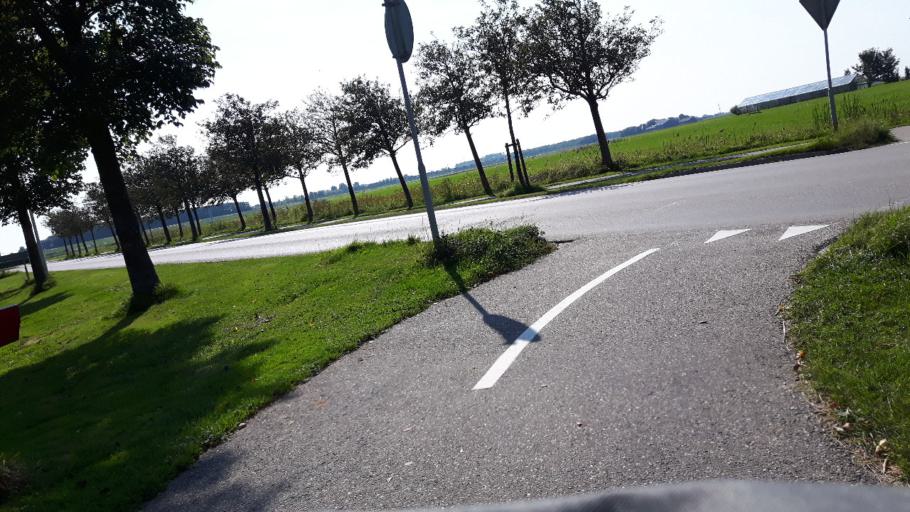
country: NL
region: Friesland
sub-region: Gemeente Franekeradeel
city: Franeker
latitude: 53.2076
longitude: 5.5423
